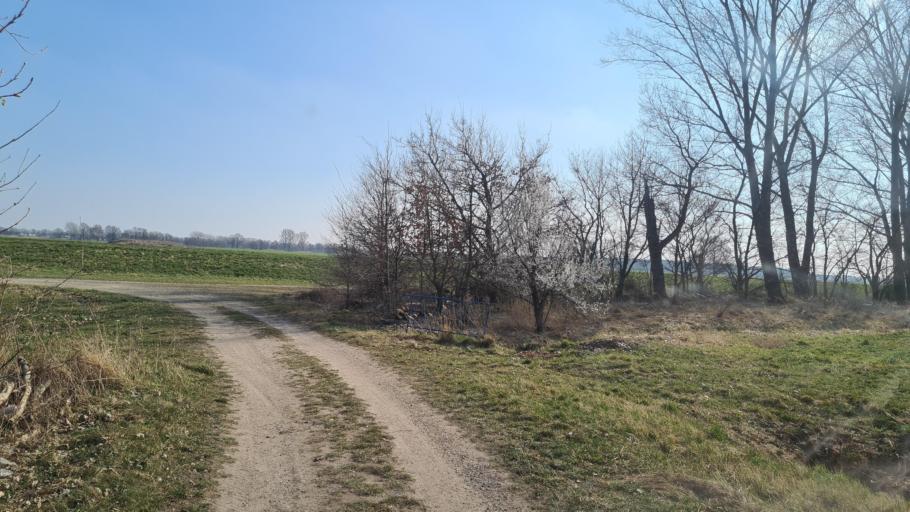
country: DE
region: Saxony
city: Nauwalde
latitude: 51.4580
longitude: 13.4345
